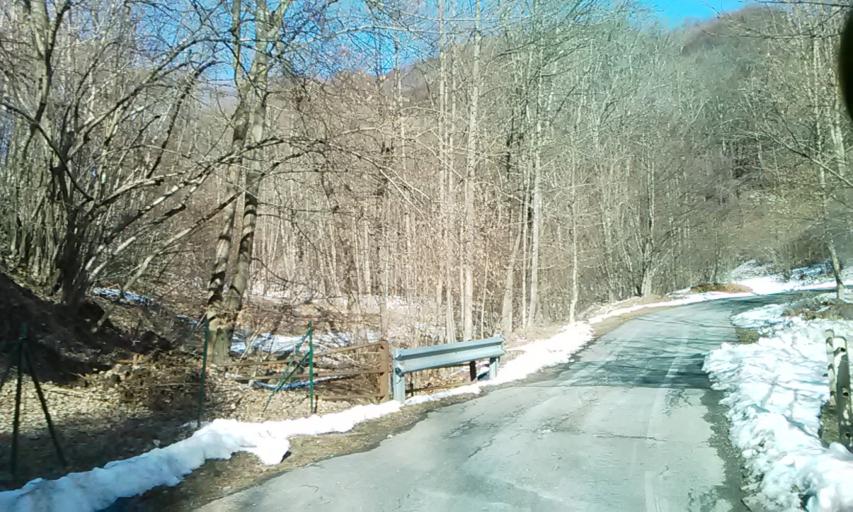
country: IT
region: Piedmont
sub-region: Provincia di Vercelli
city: Cellio
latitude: 45.7736
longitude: 8.3316
